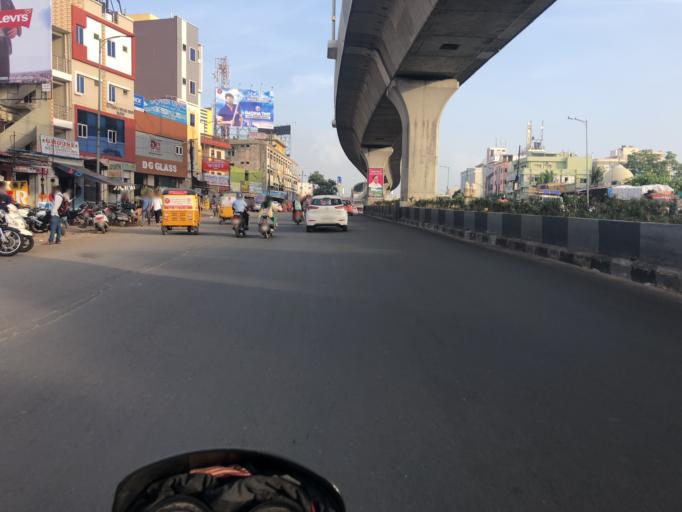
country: IN
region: Telangana
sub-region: Rangareddi
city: Kukatpalli
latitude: 17.4447
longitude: 78.4399
